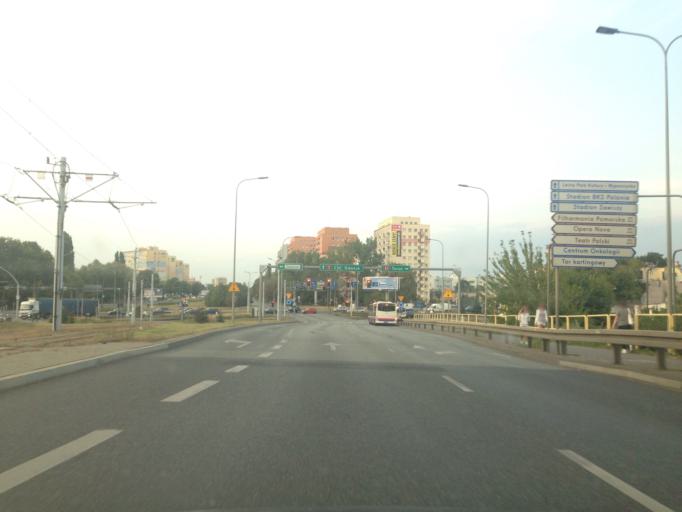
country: PL
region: Kujawsko-Pomorskie
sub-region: Bydgoszcz
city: Bydgoszcz
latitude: 53.1197
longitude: 18.0348
